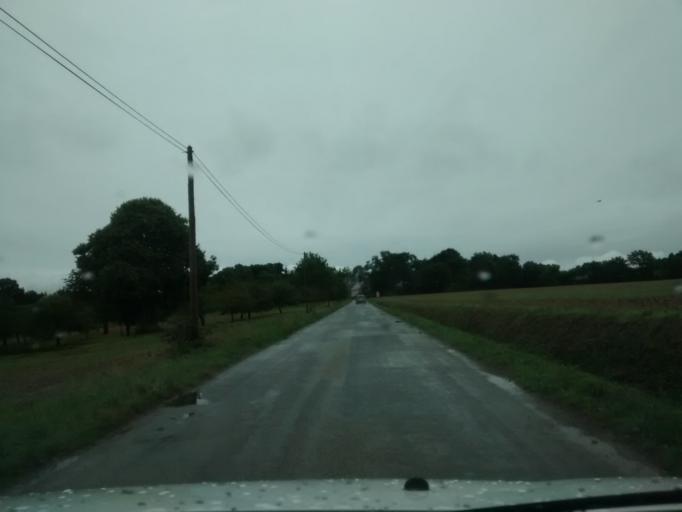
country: FR
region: Brittany
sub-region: Departement d'Ille-et-Vilaine
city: Vern-sur-Seiche
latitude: 48.0498
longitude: -1.5871
